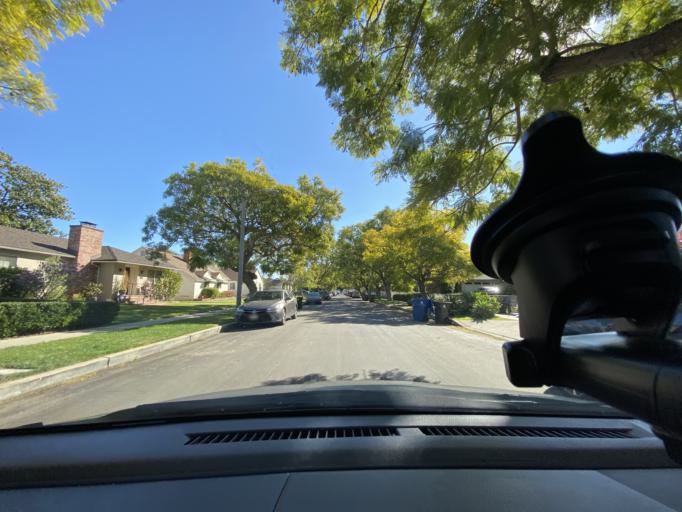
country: US
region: California
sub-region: Los Angeles County
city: Westwood, Los Angeles
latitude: 34.0208
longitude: -118.4321
